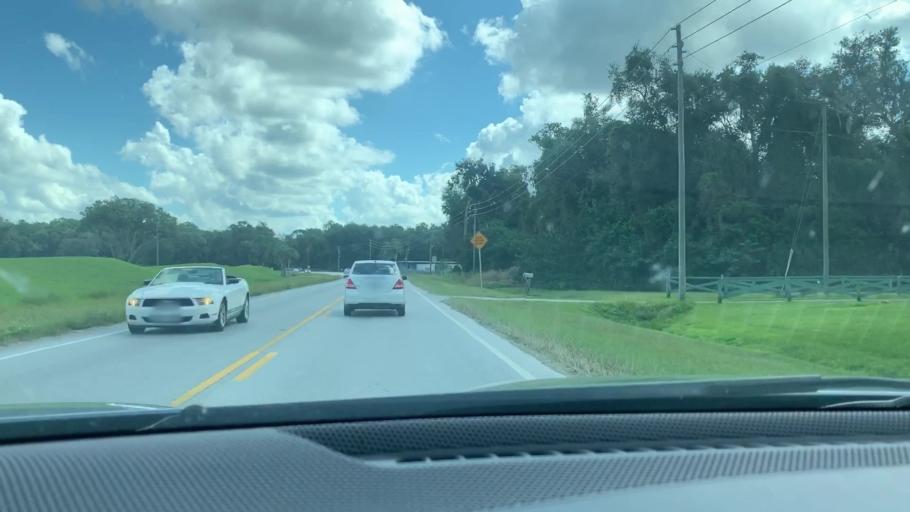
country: US
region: Florida
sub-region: Marion County
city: Ocala
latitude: 29.2673
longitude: -82.1593
